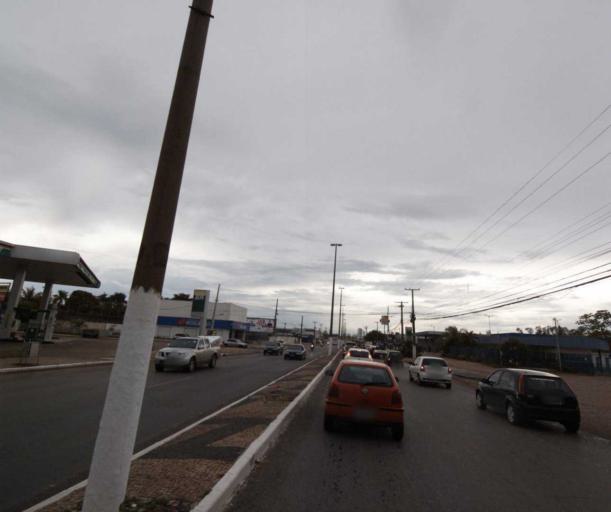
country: BR
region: Mato Grosso
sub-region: Cuiaba
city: Cuiaba
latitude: -15.6312
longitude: -56.0516
